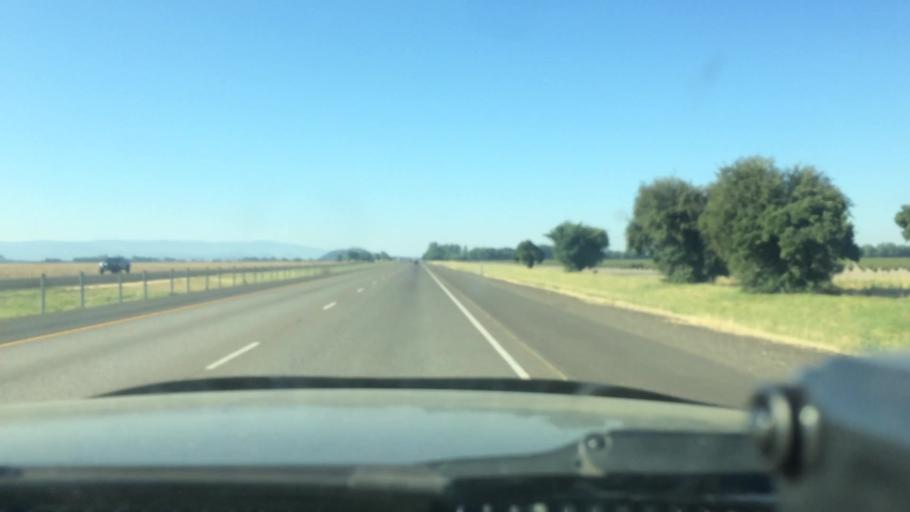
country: US
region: Oregon
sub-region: Linn County
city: Tangent
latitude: 44.5197
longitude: -123.0628
